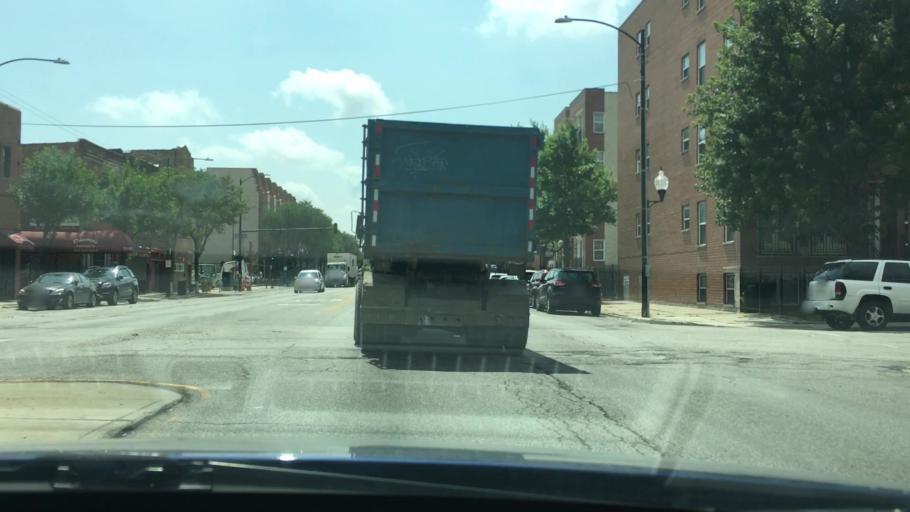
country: US
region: Illinois
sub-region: Cook County
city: Chicago
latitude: 41.8722
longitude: -87.6862
